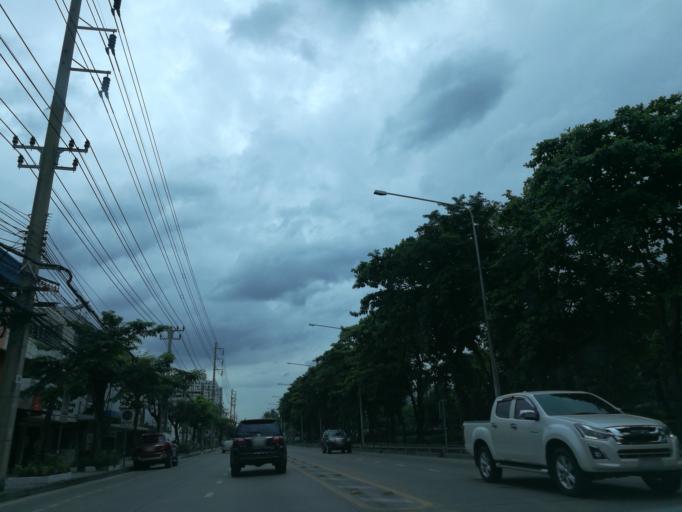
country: TH
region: Bangkok
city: Chatuchak
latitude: 13.8471
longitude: 100.5431
